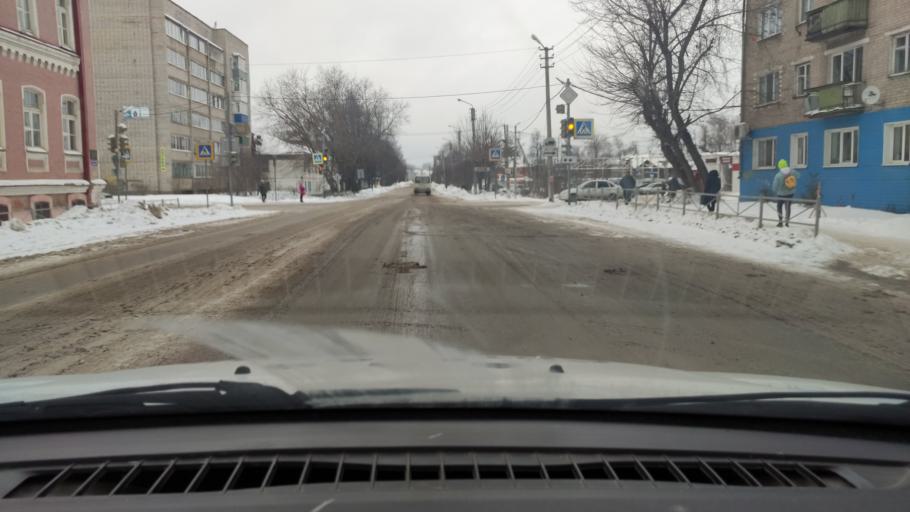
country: RU
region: Perm
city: Kungur
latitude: 57.4379
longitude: 56.9324
